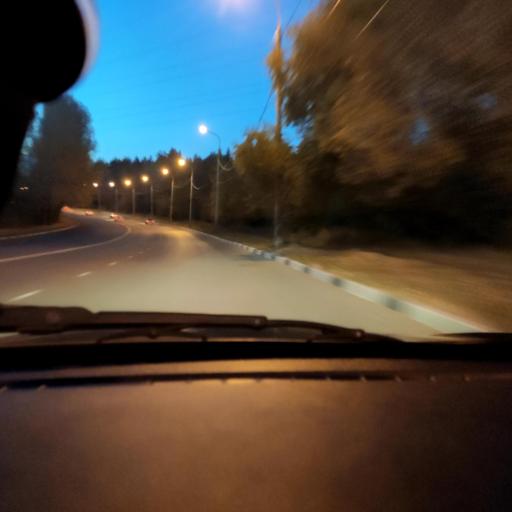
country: RU
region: Samara
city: Zhigulevsk
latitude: 53.5016
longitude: 49.4720
